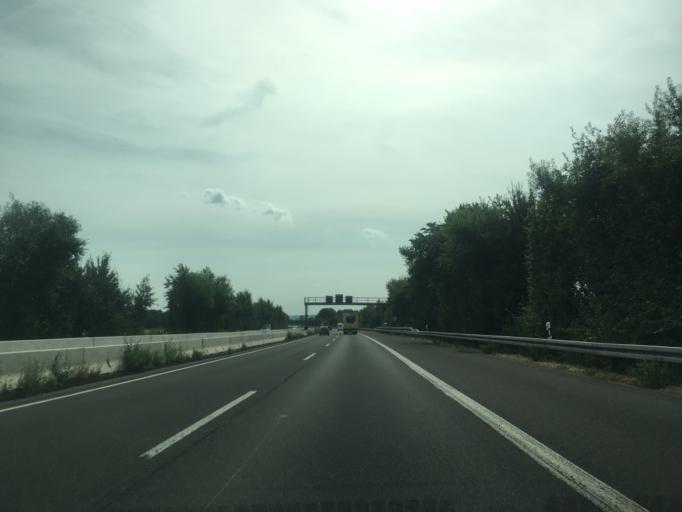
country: DE
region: North Rhine-Westphalia
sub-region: Regierungsbezirk Koln
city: Rheinbach
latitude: 50.6582
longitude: 6.9249
